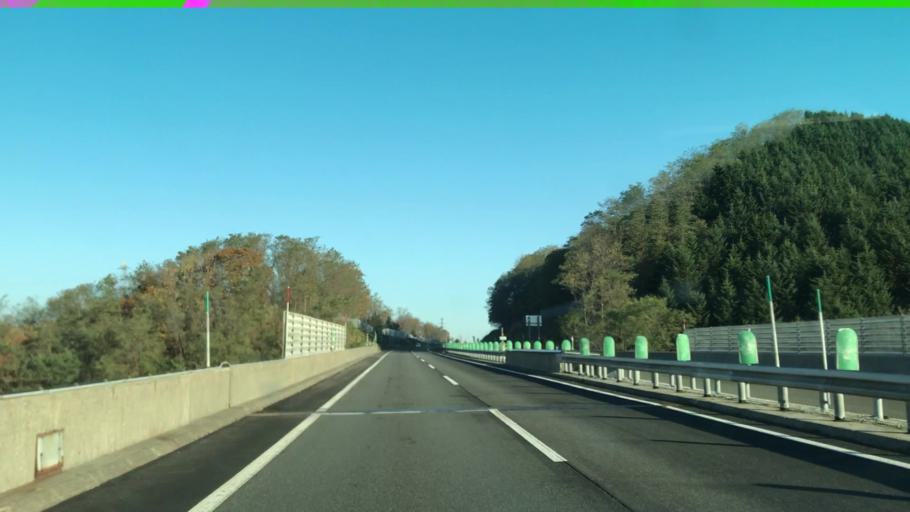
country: JP
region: Hokkaido
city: Sunagawa
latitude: 43.4178
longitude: 141.9110
